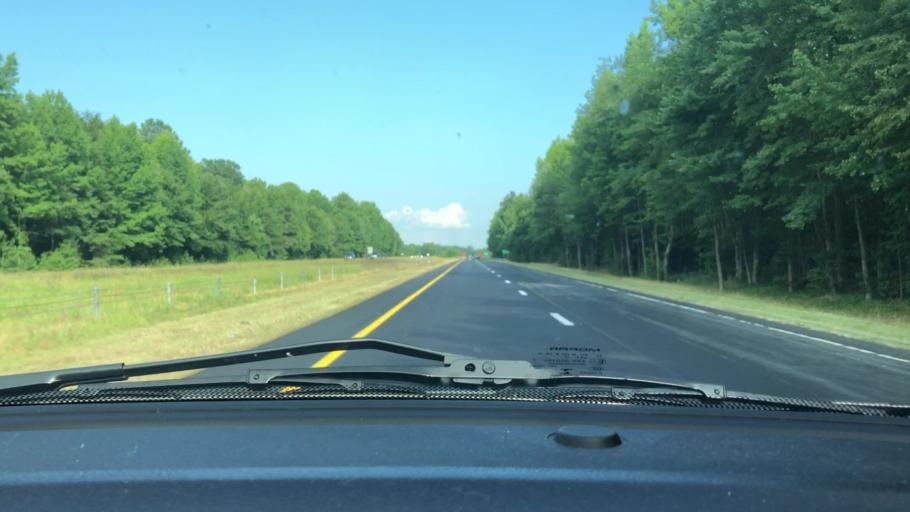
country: US
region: North Carolina
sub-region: Randolph County
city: Liberty
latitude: 35.8171
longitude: -79.5627
